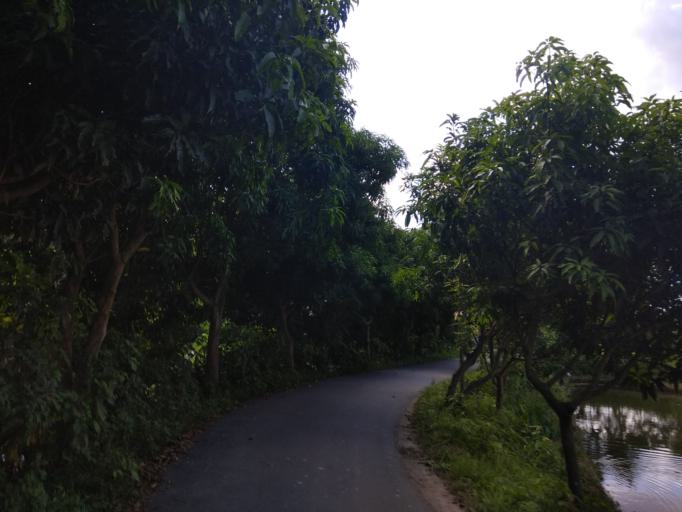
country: BD
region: Dhaka
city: Narayanganj
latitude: 23.4412
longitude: 90.4659
